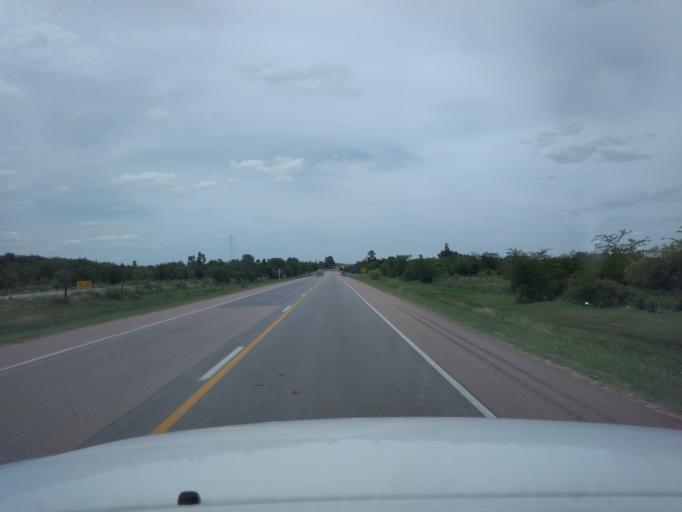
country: UY
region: Canelones
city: Canelones
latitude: -34.5045
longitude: -56.2815
